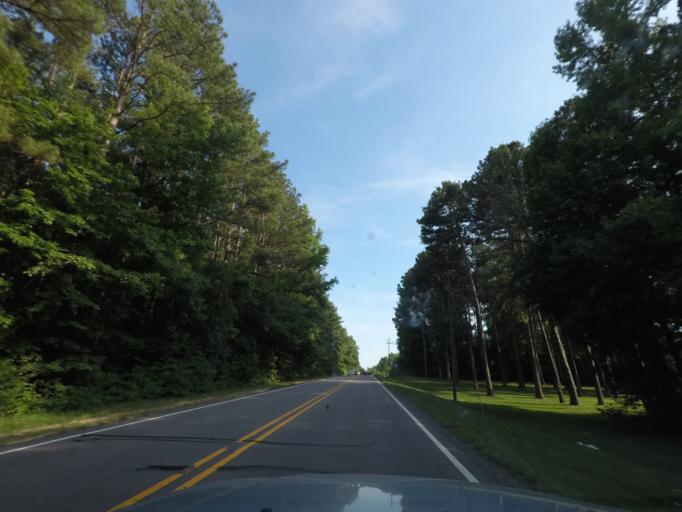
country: US
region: North Carolina
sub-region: Granville County
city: Oxford
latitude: 36.3957
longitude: -78.5926
